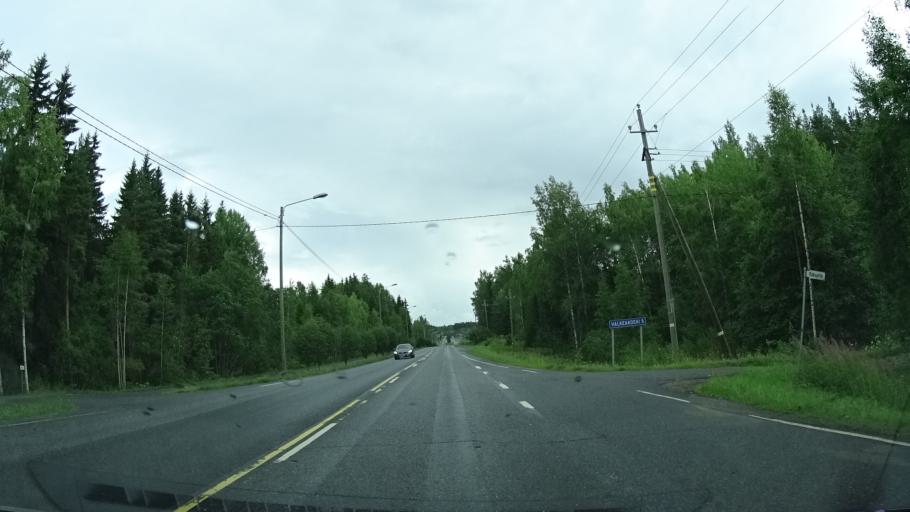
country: FI
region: Pirkanmaa
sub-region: Etelae-Pirkanmaa
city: Valkeakoski
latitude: 61.2748
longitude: 23.9767
